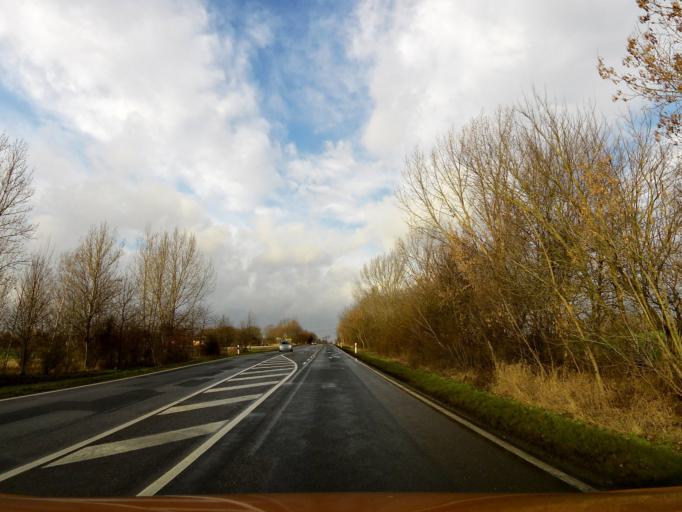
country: DE
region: Saxony-Anhalt
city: Ebendorf
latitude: 52.1896
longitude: 11.5668
